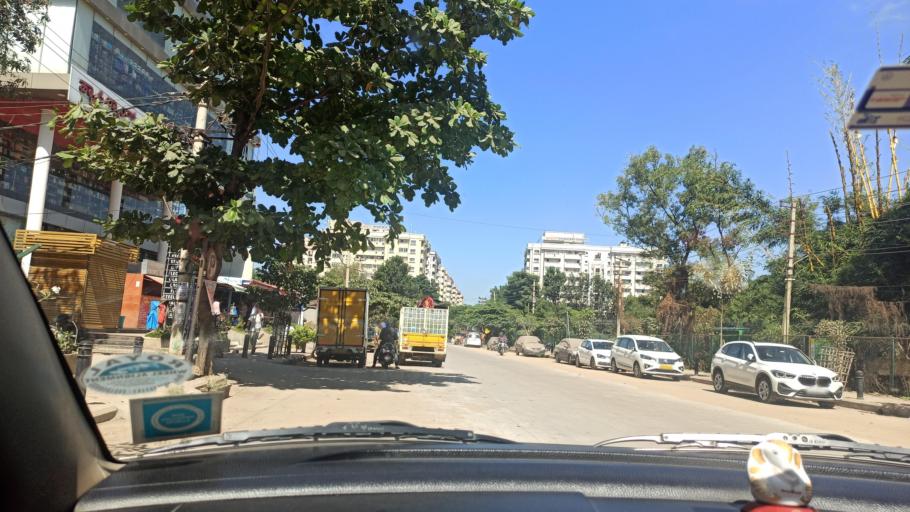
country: IN
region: Karnataka
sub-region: Bangalore Urban
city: Bangalore
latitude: 12.9219
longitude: 77.6654
